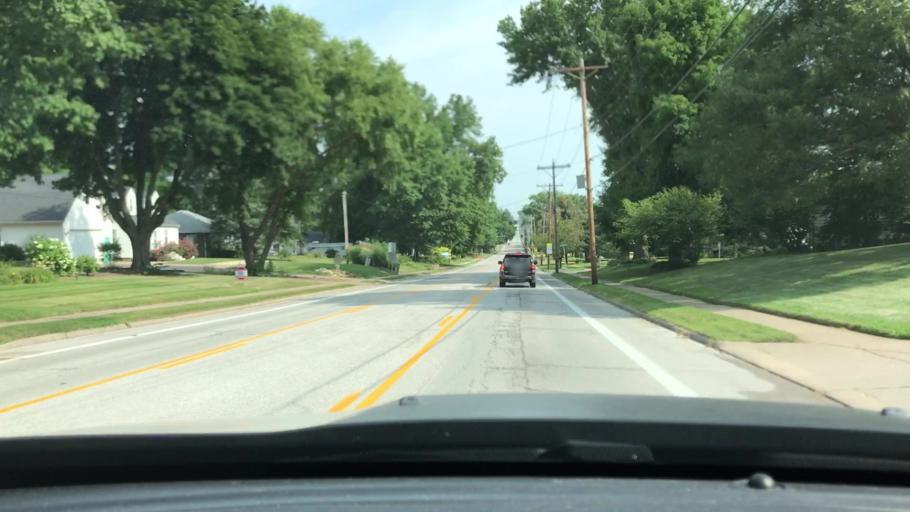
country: US
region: Iowa
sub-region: Scott County
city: Bettendorf
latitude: 41.5463
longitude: -90.5417
